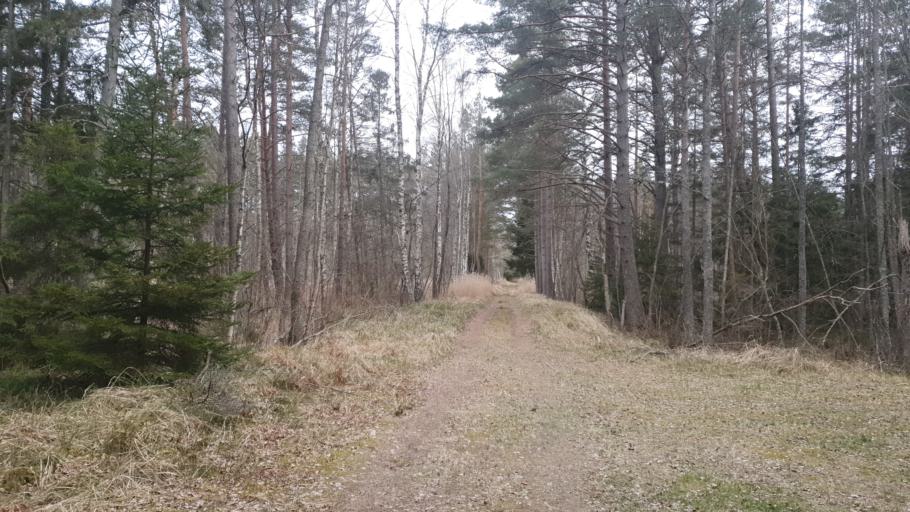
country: LV
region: Ventspils
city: Ventspils
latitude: 57.5753
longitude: 21.7594
